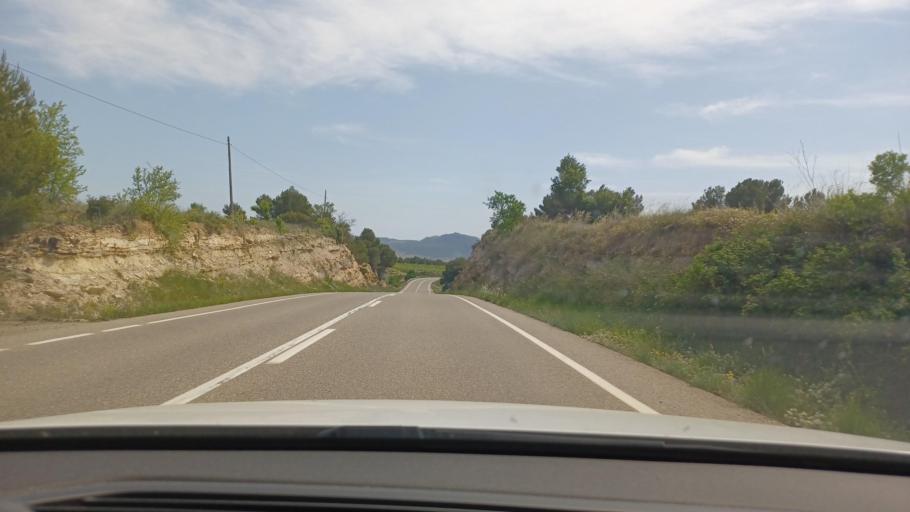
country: ES
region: Catalonia
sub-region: Provincia de Tarragona
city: Vilalba dels Arcs
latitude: 41.0937
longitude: 0.4187
